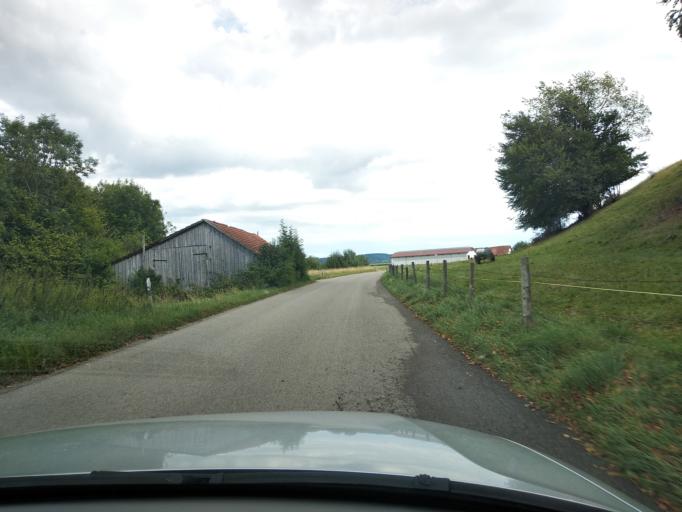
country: DE
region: Bavaria
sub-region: Swabia
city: Woringen
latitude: 47.8979
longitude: 10.2173
